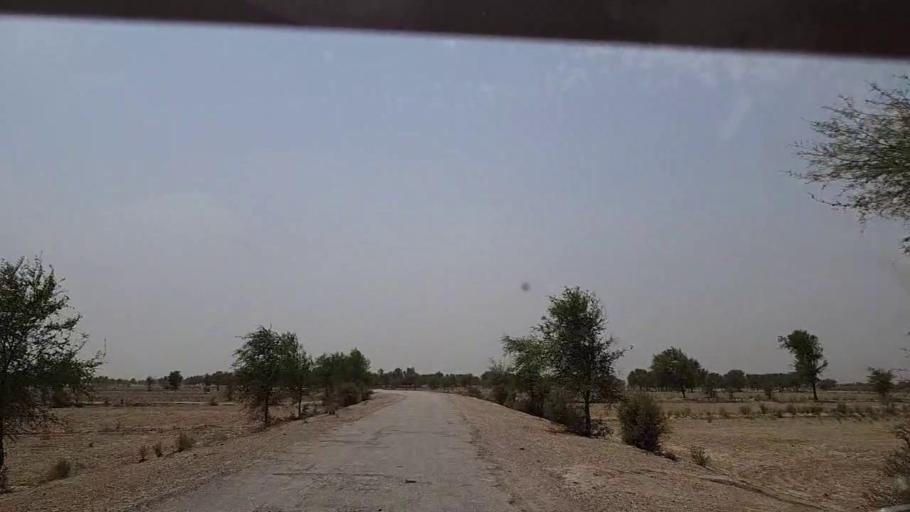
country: PK
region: Sindh
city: Khairpur Nathan Shah
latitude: 27.0165
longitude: 67.5982
